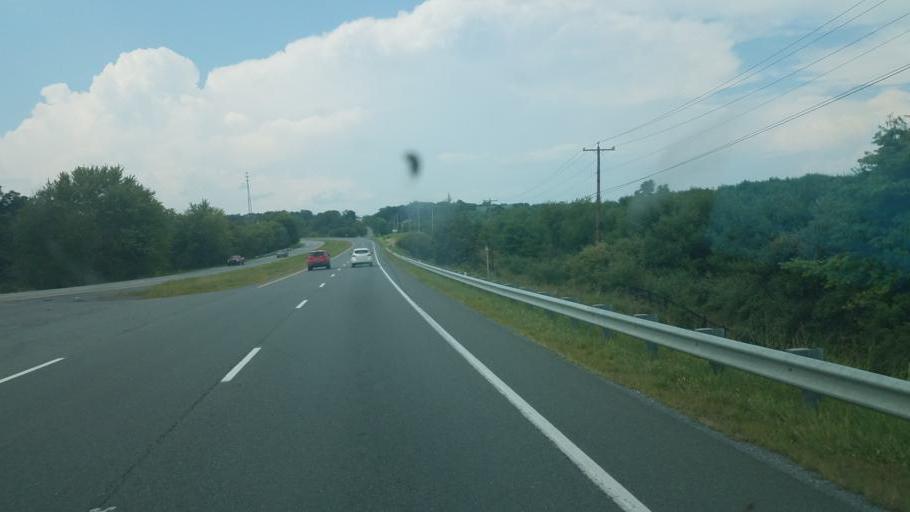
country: US
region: Virginia
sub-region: Frederick County
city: Shawnee Land
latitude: 39.3103
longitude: -78.2887
